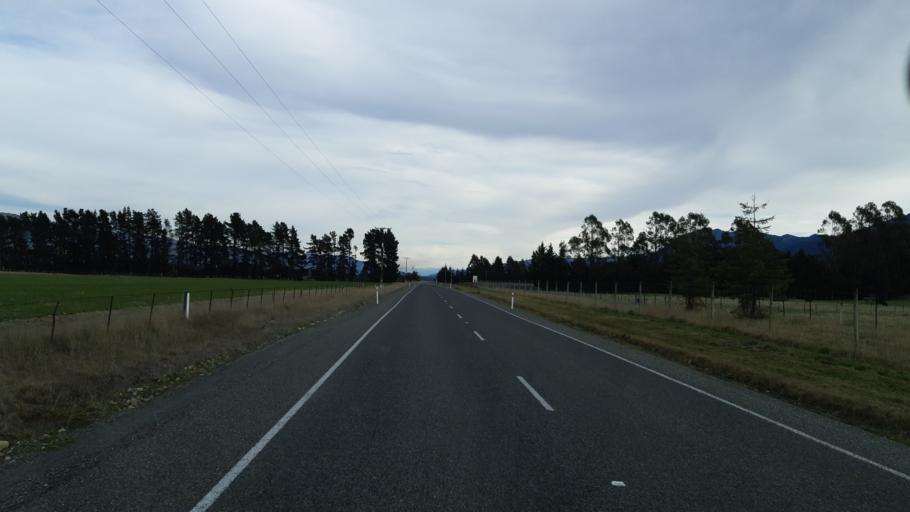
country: NZ
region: Tasman
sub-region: Tasman District
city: Richmond
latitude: -41.6031
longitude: 173.4177
